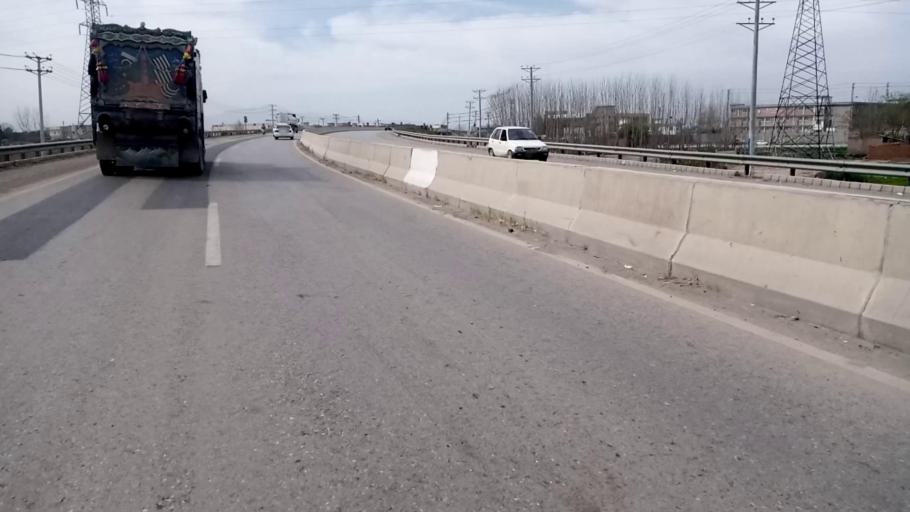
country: PK
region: Khyber Pakhtunkhwa
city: Peshawar
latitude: 34.0380
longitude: 71.6229
